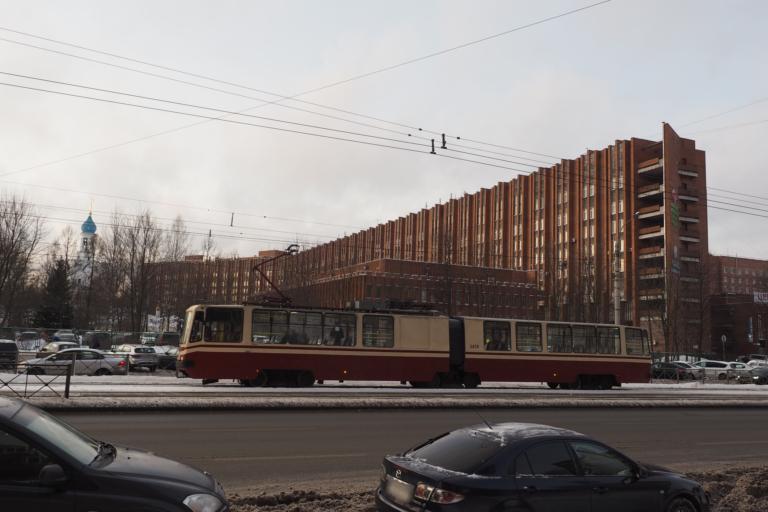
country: RU
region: St.-Petersburg
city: Sosnovka
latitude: 60.0368
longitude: 30.3646
